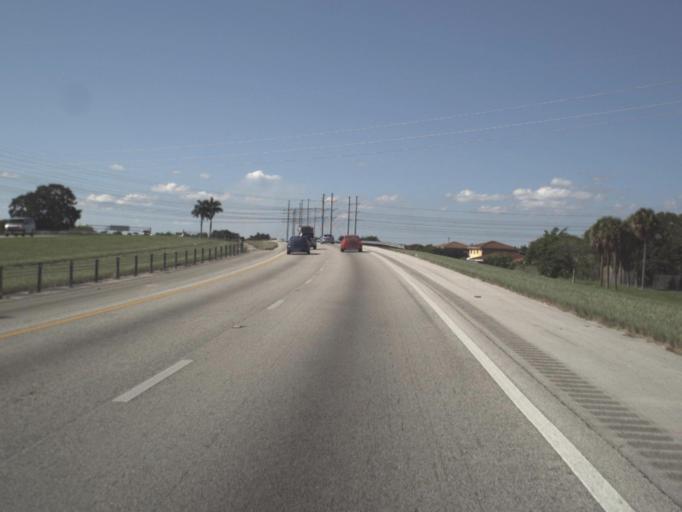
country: US
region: Florida
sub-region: Miami-Dade County
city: Princeton
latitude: 25.5276
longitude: -80.3955
